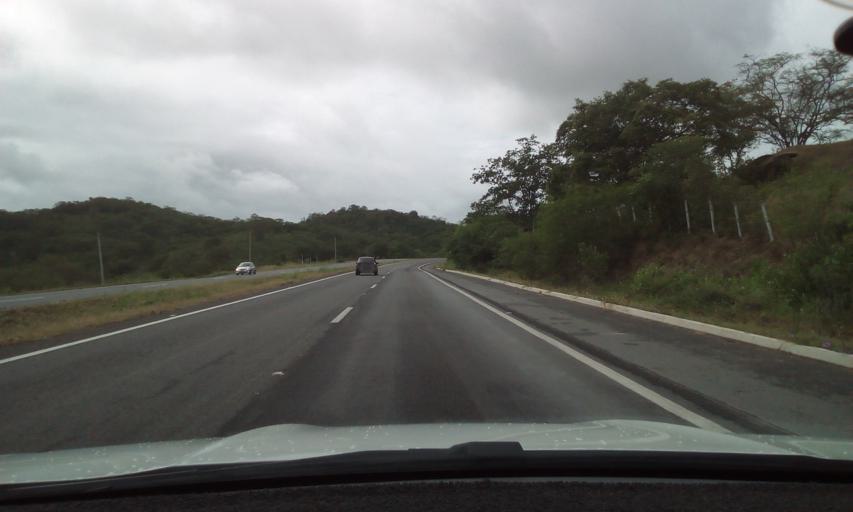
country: BR
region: Paraiba
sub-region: Massaranduba
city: Massaranduba
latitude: -7.2761
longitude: -35.7778
